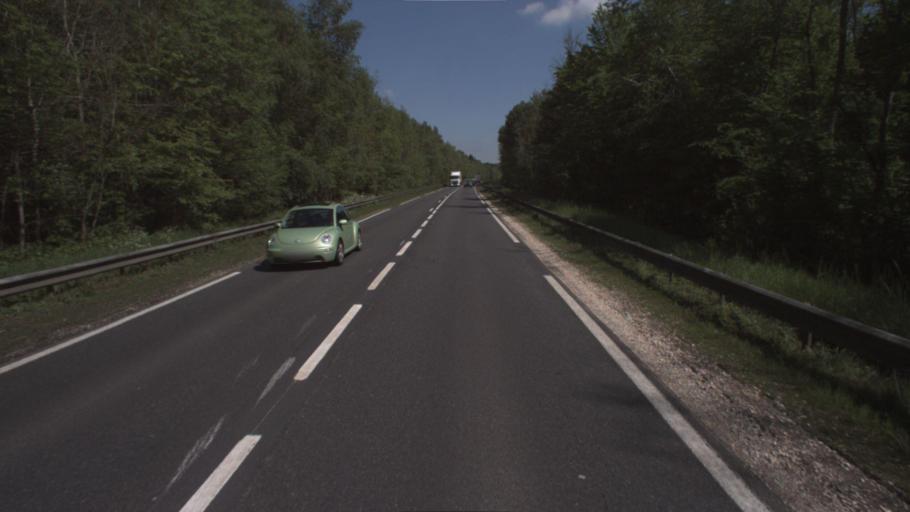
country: FR
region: Ile-de-France
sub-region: Departement de Seine-et-Marne
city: Chaumes-en-Brie
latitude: 48.6828
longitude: 2.8151
